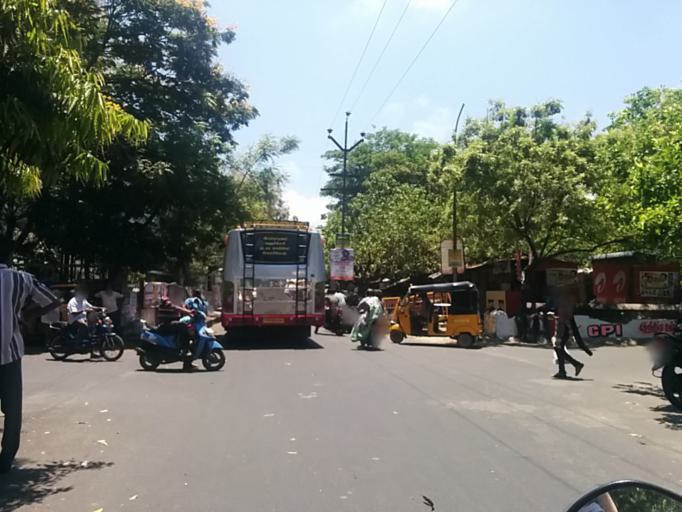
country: IN
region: Pondicherry
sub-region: Puducherry
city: Puducherry
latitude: 11.9346
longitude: 79.8327
